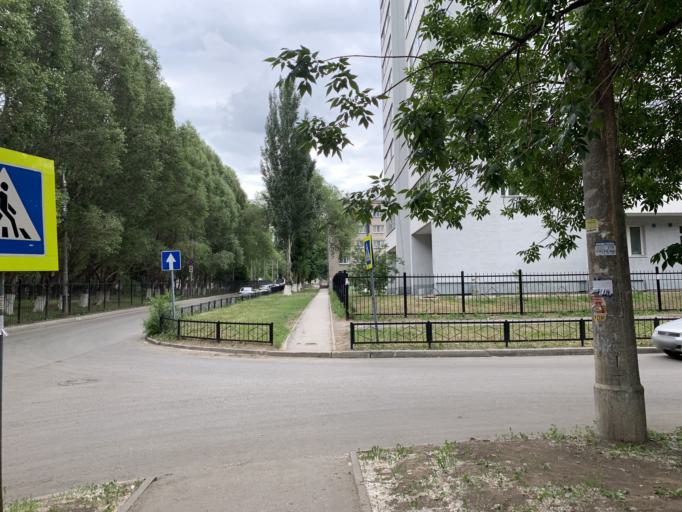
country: RU
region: Samara
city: Samara
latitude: 53.2129
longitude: 50.1739
